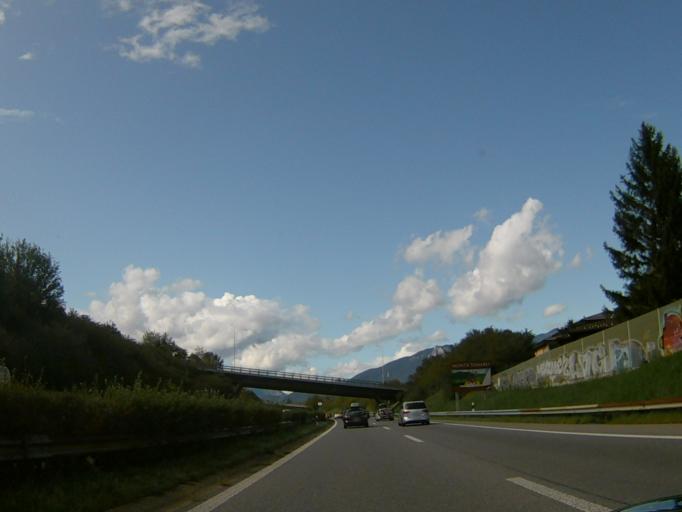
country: CH
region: Ticino
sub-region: Bellinzona District
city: Cadenazzo
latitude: 46.1168
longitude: 8.9266
